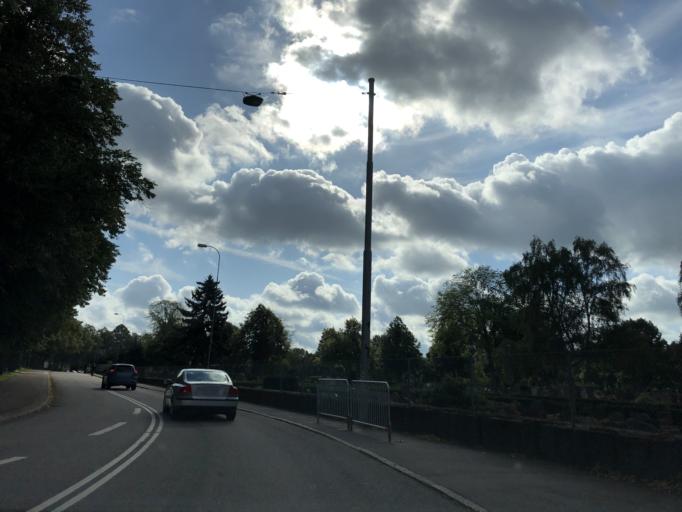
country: SE
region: Vaestra Goetaland
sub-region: Goteborg
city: Goeteborg
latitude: 57.7168
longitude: 12.0134
